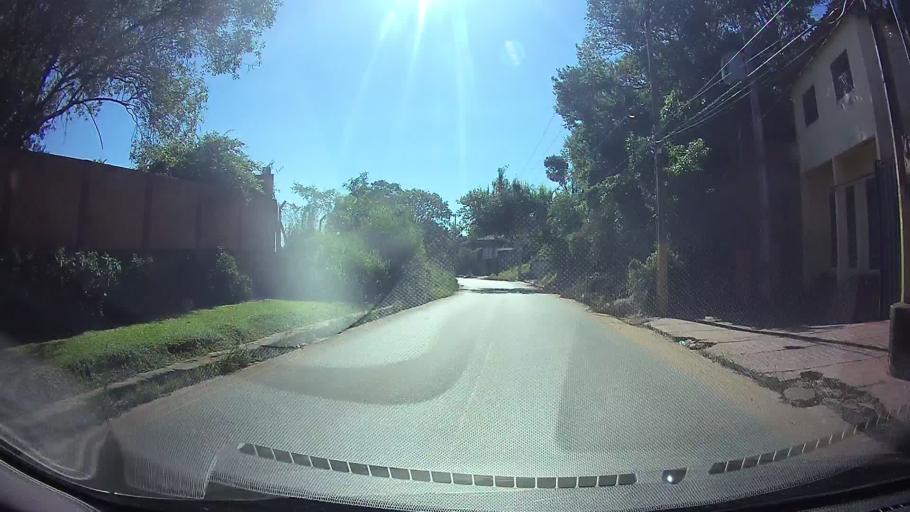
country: PY
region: Central
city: Fernando de la Mora
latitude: -25.2966
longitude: -57.5291
